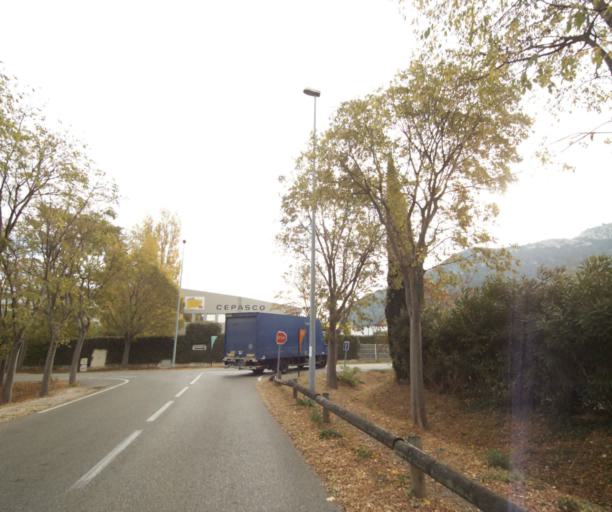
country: FR
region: Provence-Alpes-Cote d'Azur
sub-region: Departement des Bouches-du-Rhone
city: Gemenos
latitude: 43.2798
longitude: 5.6175
